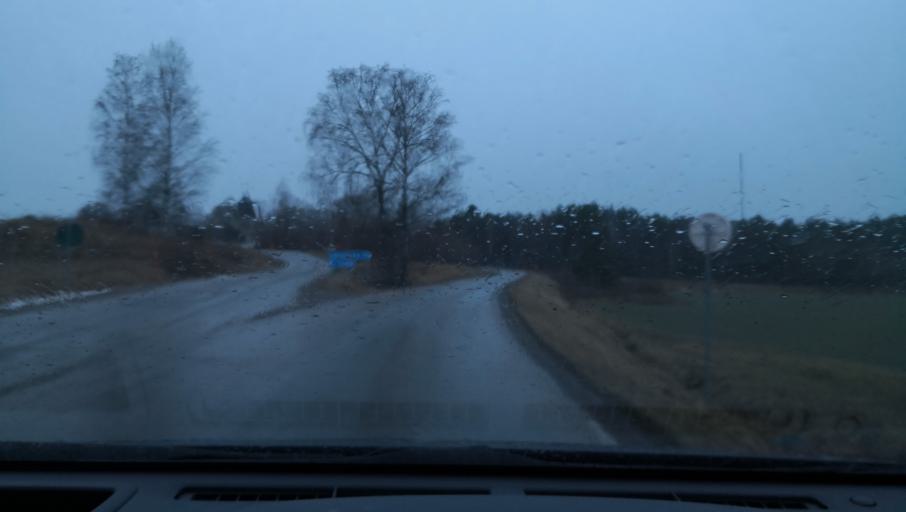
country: SE
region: Soedermanland
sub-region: Eskilstuna Kommun
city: Arla
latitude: 59.3991
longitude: 16.6778
